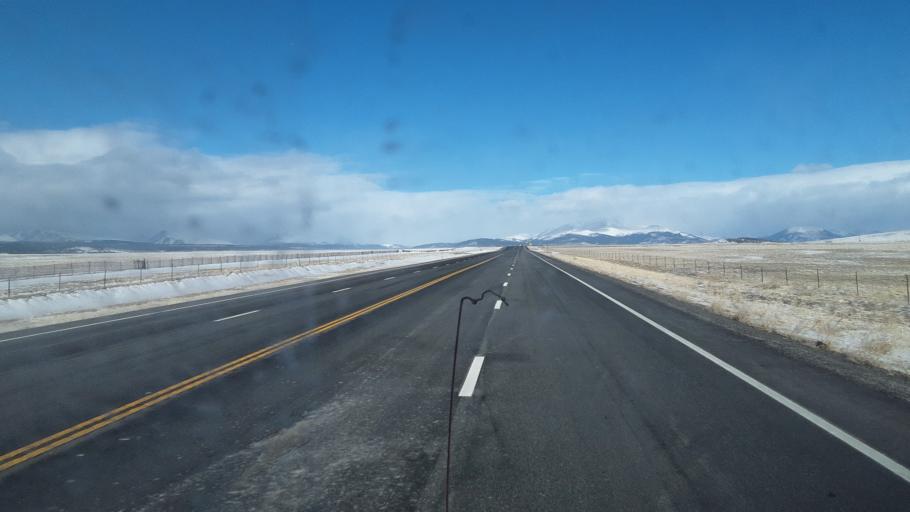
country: US
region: Colorado
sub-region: Park County
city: Fairplay
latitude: 39.1385
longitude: -105.9963
